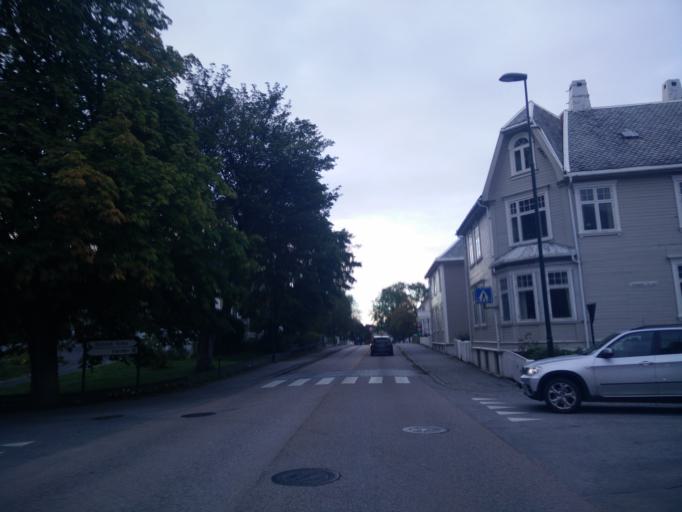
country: NO
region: More og Romsdal
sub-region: Kristiansund
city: Kristiansund
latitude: 63.1163
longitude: 7.7248
